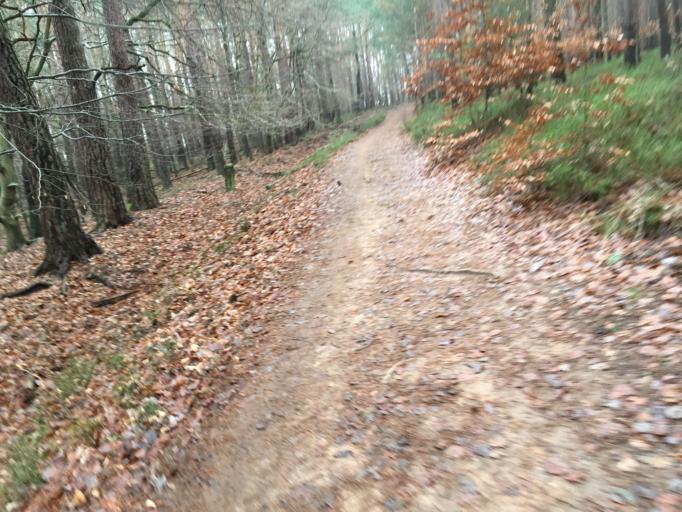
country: DE
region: Rheinland-Pfalz
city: Neustadt
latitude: 49.3347
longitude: 8.1082
